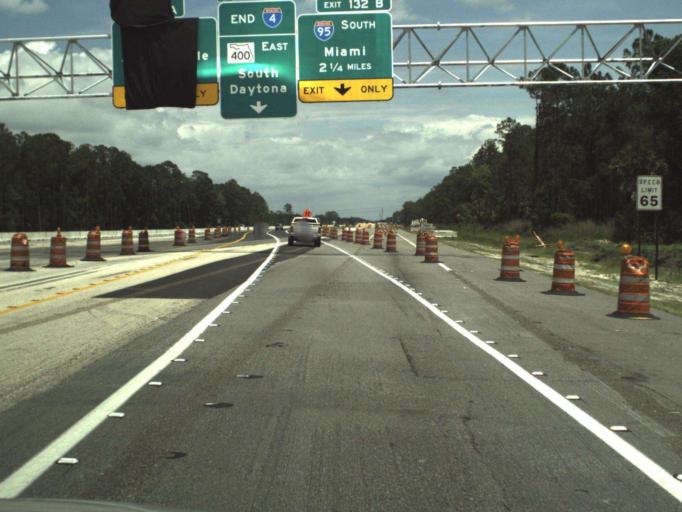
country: US
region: Florida
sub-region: Volusia County
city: Samsula-Spruce Creek
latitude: 29.1391
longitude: -81.1137
